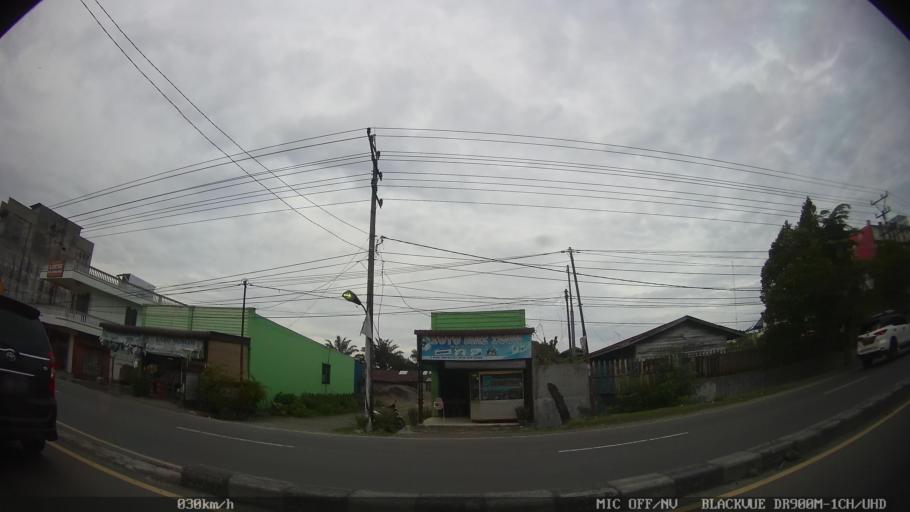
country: ID
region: North Sumatra
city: Sunggal
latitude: 3.5993
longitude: 98.5773
